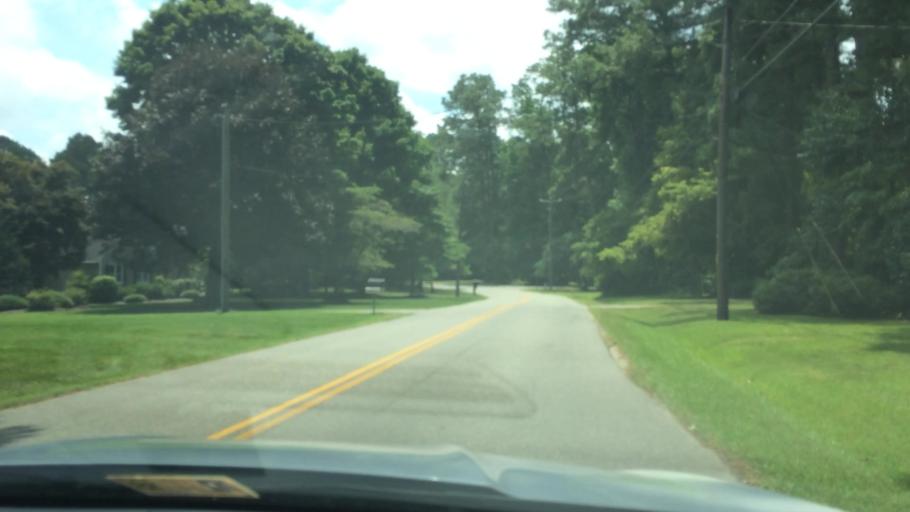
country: US
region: Virginia
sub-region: York County
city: Yorktown
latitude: 37.2074
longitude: -76.4827
